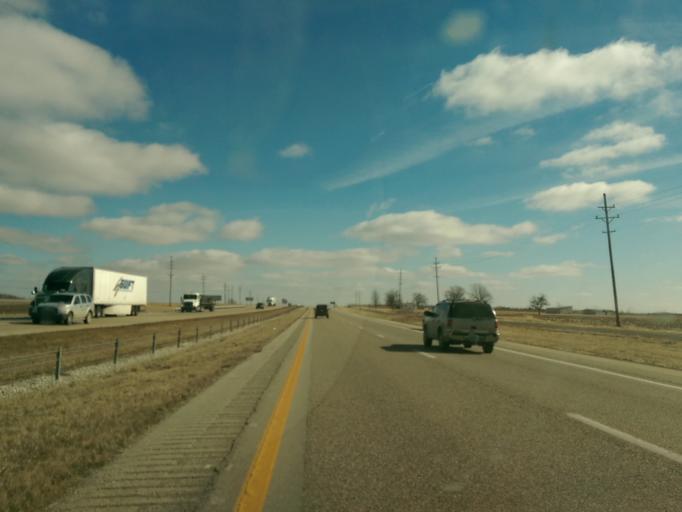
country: US
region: Missouri
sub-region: Montgomery County
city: Montgomery City
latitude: 38.8952
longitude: -91.4411
